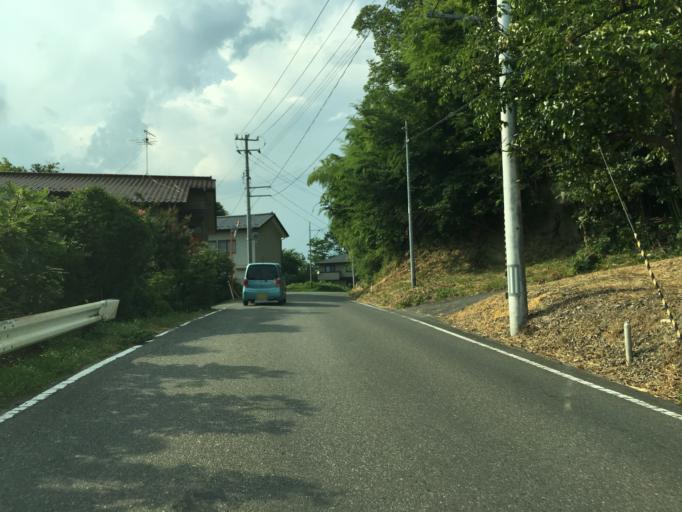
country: JP
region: Fukushima
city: Motomiya
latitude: 37.4591
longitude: 140.4241
